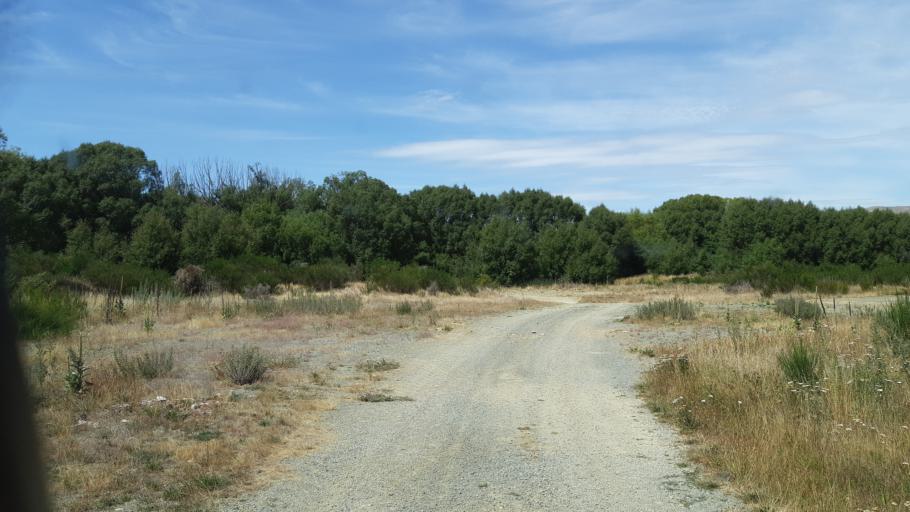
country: NZ
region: Otago
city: Oamaru
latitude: -44.6606
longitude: 170.6002
